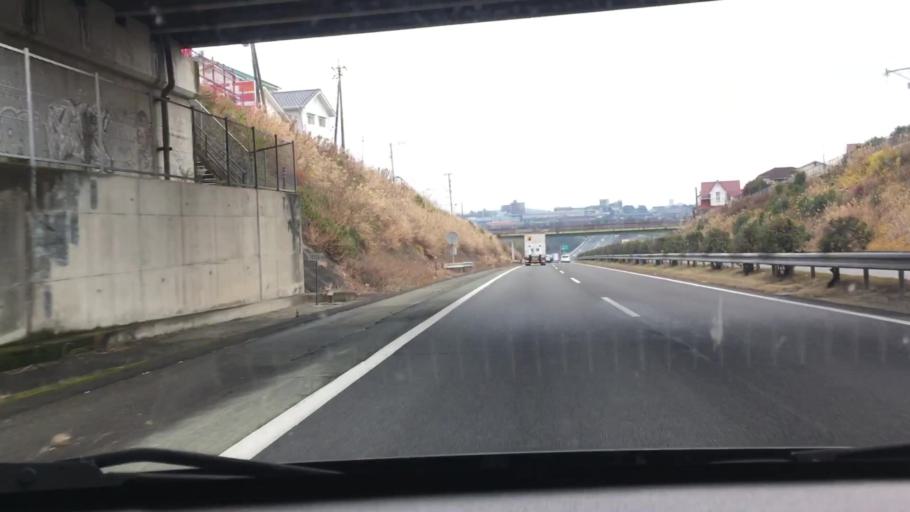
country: JP
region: Kumamoto
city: Kumamoto
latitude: 32.8482
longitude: 130.7680
